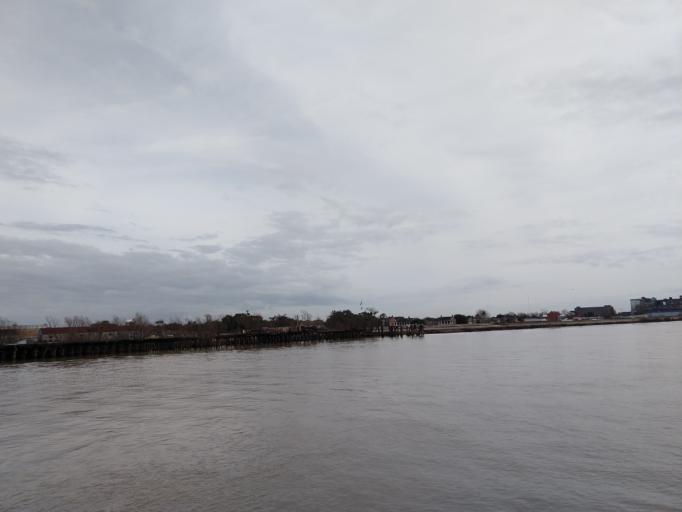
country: US
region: Louisiana
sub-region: Saint Bernard Parish
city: Arabi
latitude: 29.9492
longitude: -90.0152
